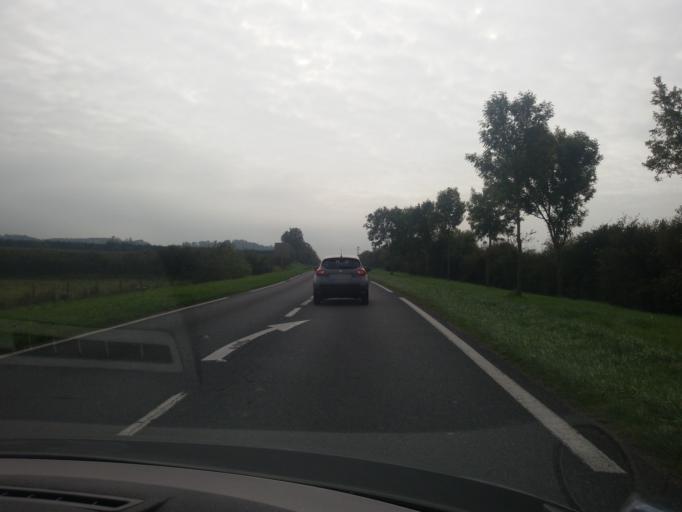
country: FR
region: Lower Normandy
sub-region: Departement du Calvados
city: Dives-sur-Mer
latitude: 49.2648
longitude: -0.1047
